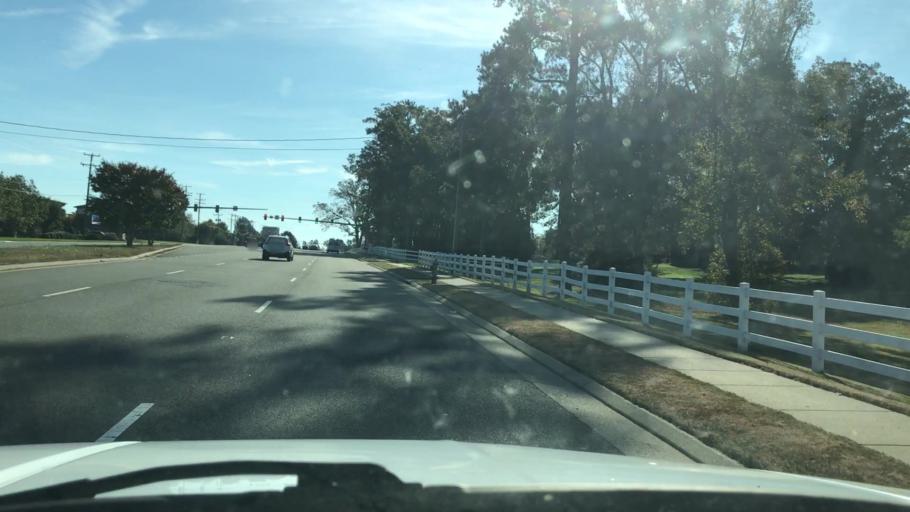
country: US
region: Virginia
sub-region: Henrico County
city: Short Pump
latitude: 37.6575
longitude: -77.6309
